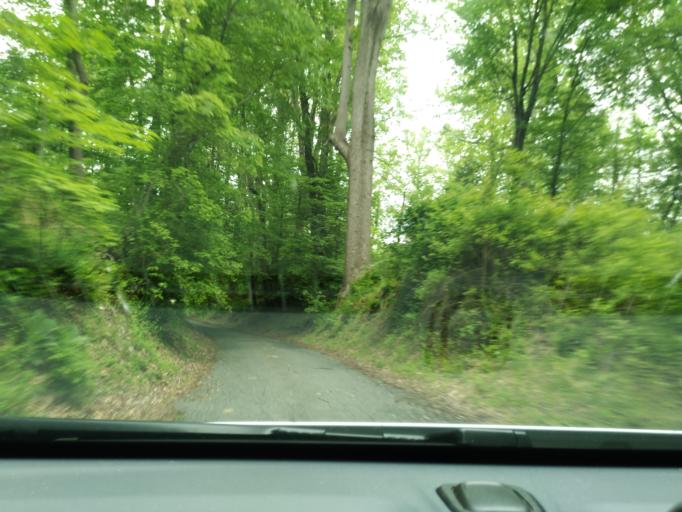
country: US
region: Maryland
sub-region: Prince George's County
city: Marlboro Meadows
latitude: 38.8585
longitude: -76.7099
